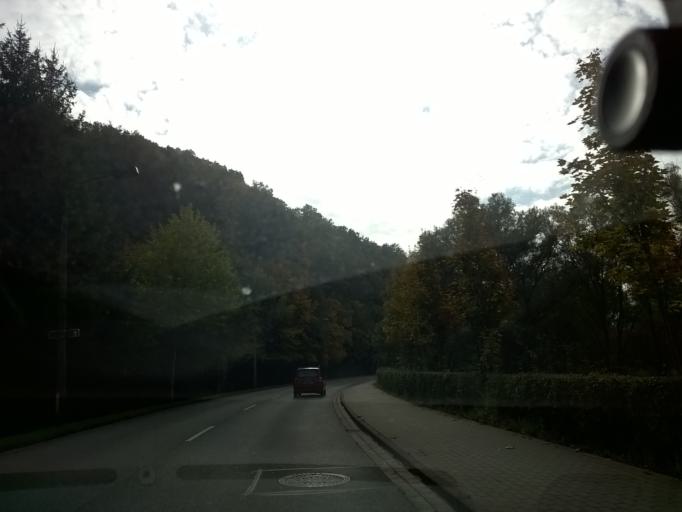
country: DE
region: Thuringia
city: Harzungen
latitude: 51.5287
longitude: 10.7833
